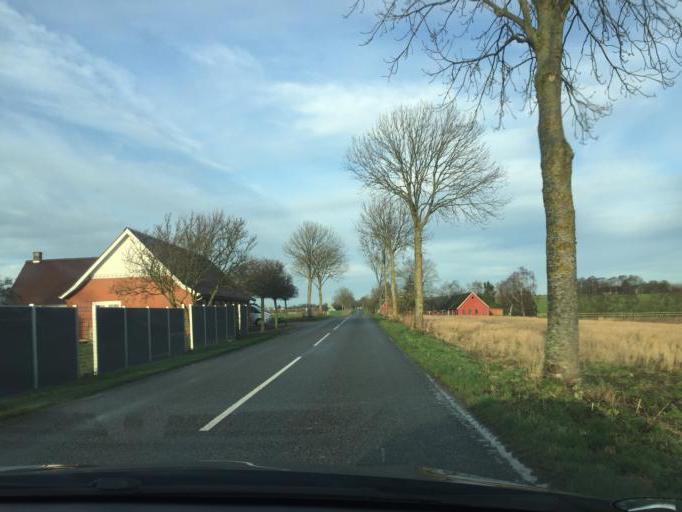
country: DK
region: South Denmark
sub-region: Faaborg-Midtfyn Kommune
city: Ringe
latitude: 55.1898
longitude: 10.4085
